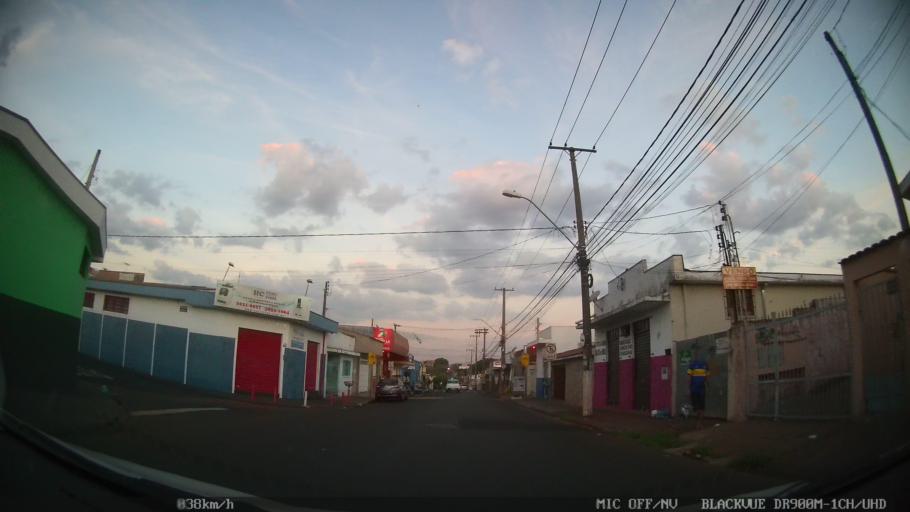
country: BR
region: Sao Paulo
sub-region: Ribeirao Preto
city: Ribeirao Preto
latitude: -21.1513
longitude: -47.8121
